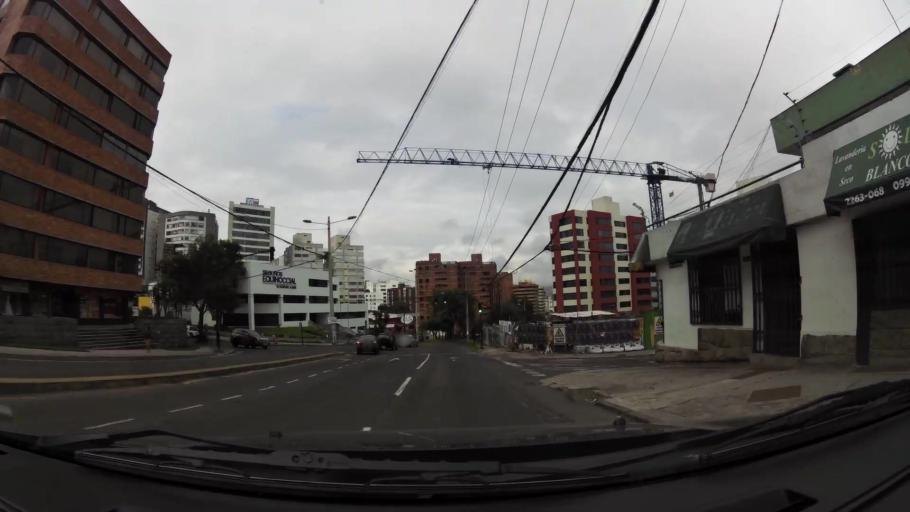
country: EC
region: Pichincha
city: Quito
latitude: -0.1854
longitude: -78.4776
